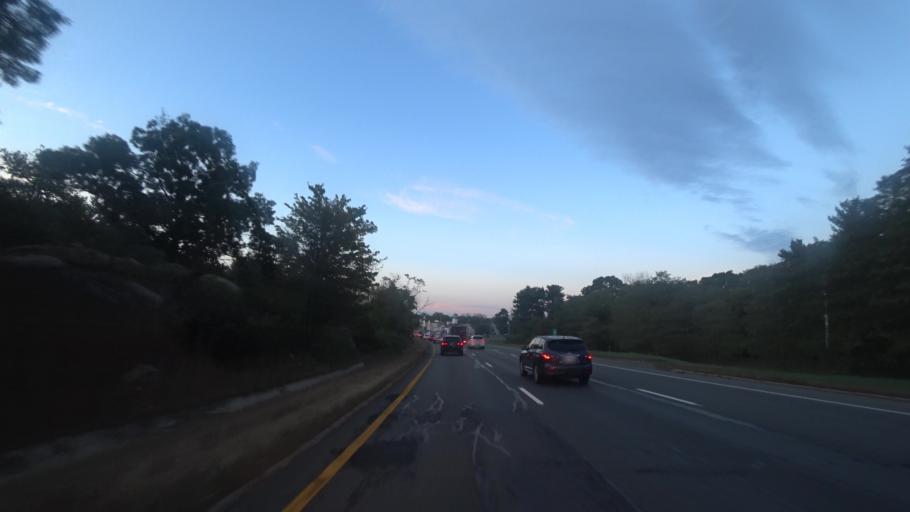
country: US
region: Massachusetts
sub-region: Essex County
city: Saugus
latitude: 42.5076
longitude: -71.0132
